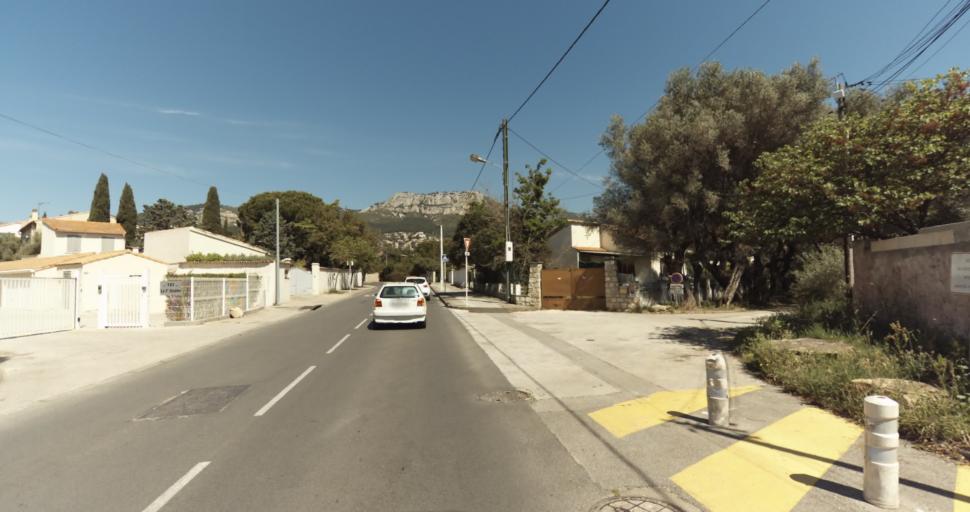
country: FR
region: Provence-Alpes-Cote d'Azur
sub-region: Departement du Var
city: Toulon
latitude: 43.1406
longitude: 5.9035
